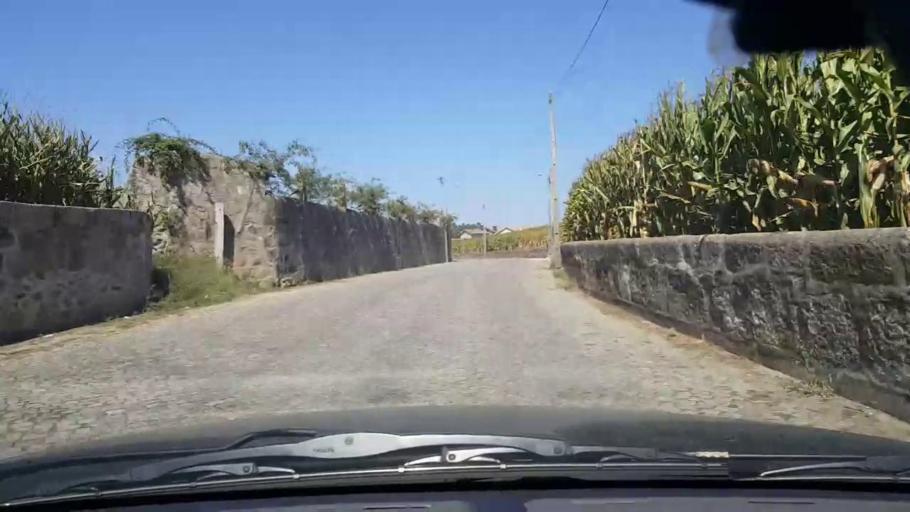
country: PT
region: Porto
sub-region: Matosinhos
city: Lavra
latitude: 41.2790
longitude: -8.7024
